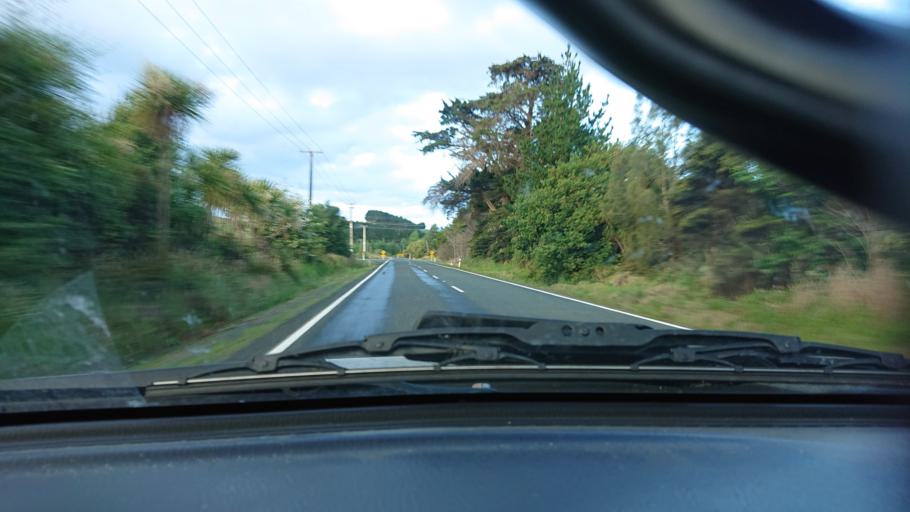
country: NZ
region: Auckland
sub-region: Auckland
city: Parakai
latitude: -36.4855
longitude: 174.4496
